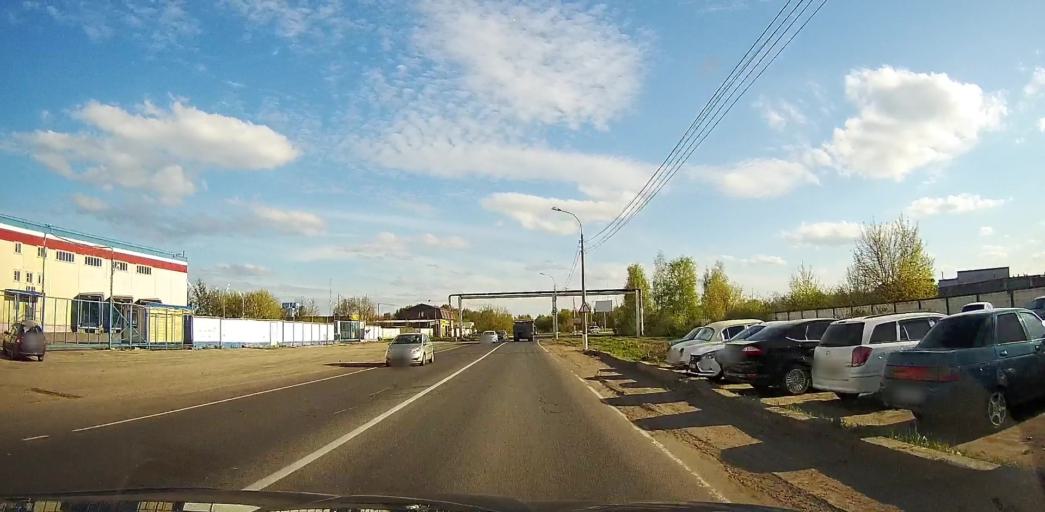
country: RU
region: Moskovskaya
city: Ramenskoye
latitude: 55.5624
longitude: 38.2636
